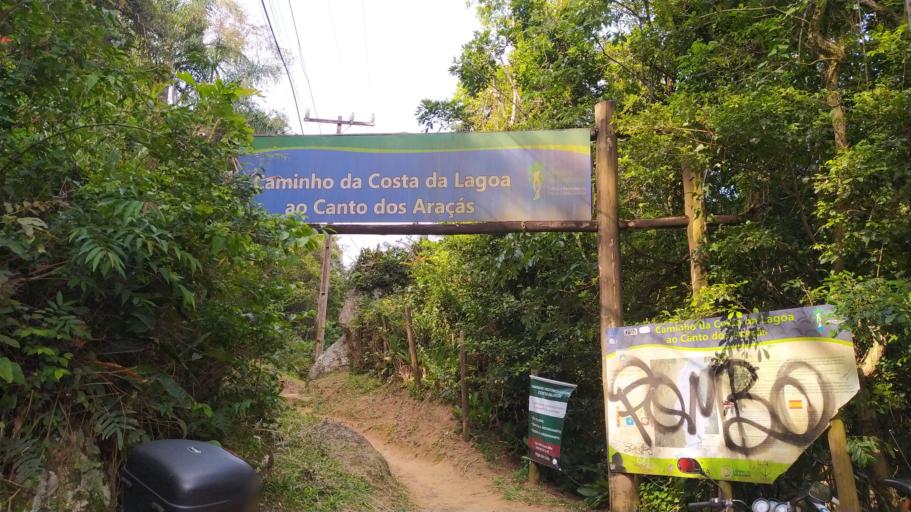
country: BR
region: Santa Catarina
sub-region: Florianopolis
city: Lagoa
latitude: -27.5809
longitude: -48.4576
